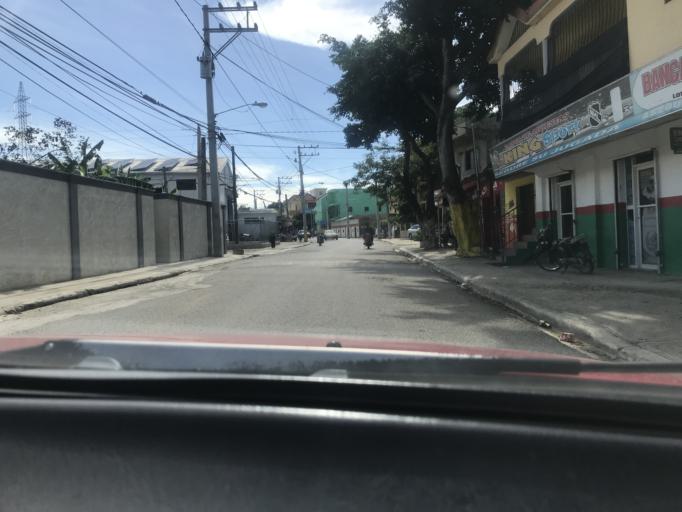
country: DO
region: Santiago
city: Licey al Medio
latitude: 19.4061
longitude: -70.6306
